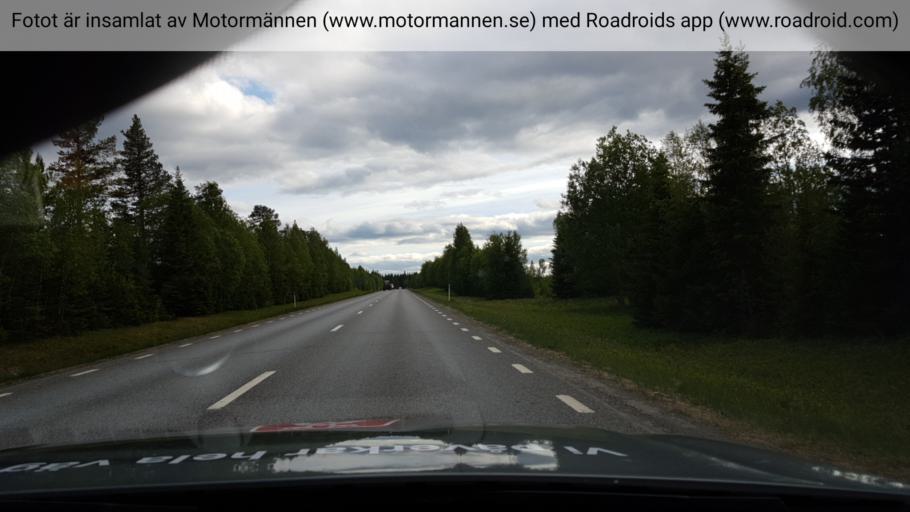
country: SE
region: Jaemtland
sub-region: Stroemsunds Kommun
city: Stroemsund
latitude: 63.5147
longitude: 15.2891
